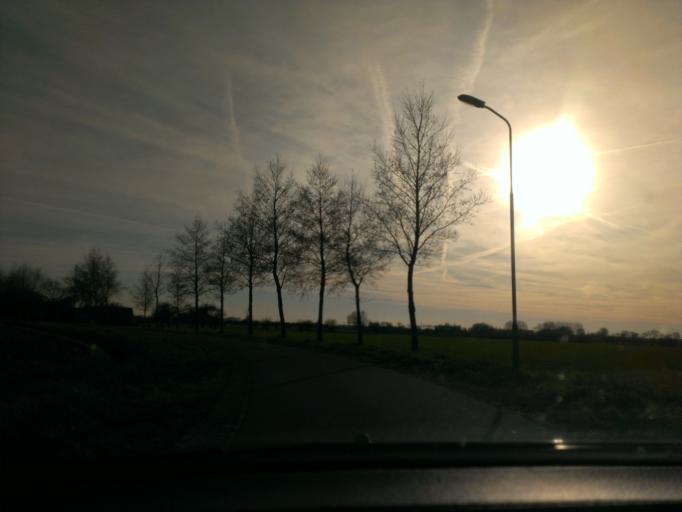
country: NL
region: Overijssel
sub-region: Gemeente Olst-Wijhe
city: Wijhe
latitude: 52.3946
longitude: 6.1134
